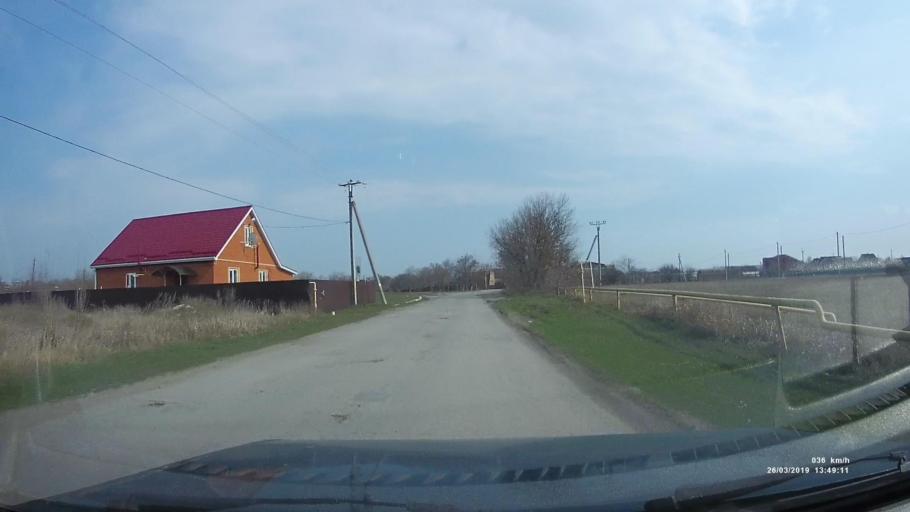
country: RU
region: Rostov
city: Novobessergenovka
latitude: 47.1911
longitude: 38.8642
